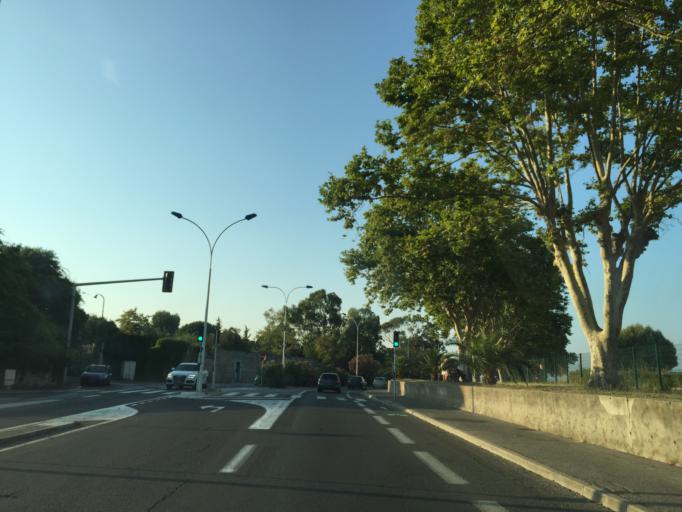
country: FR
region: Provence-Alpes-Cote d'Azur
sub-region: Departement des Alpes-Maritimes
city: Antibes
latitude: 43.5905
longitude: 7.1244
